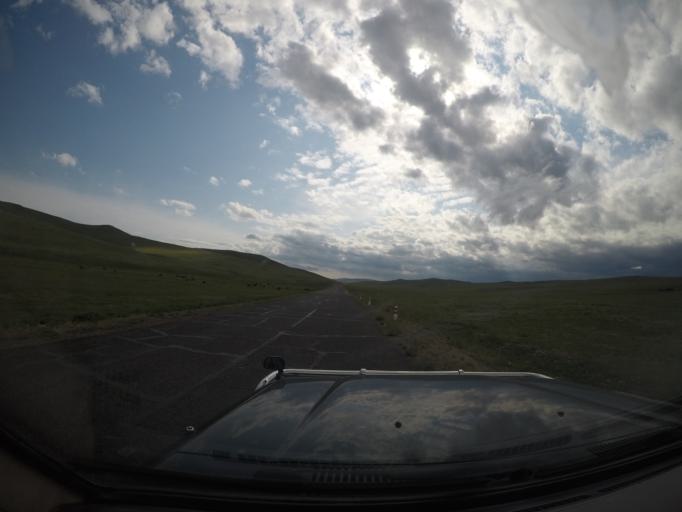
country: MN
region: Hentiy
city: Modot
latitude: 47.7952
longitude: 108.6883
